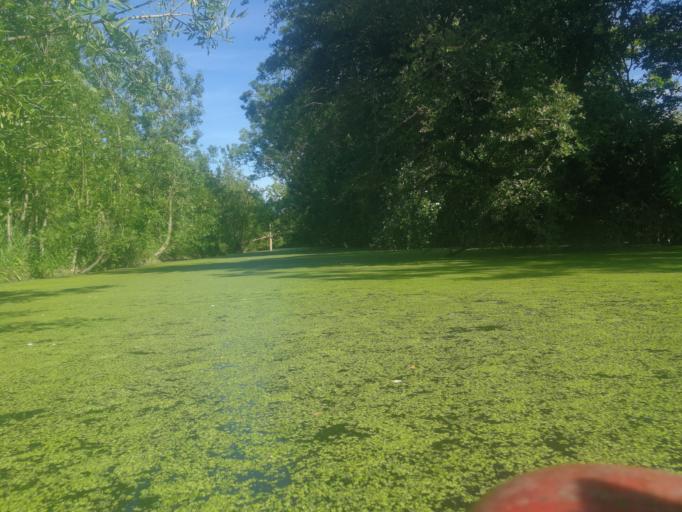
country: FR
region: Poitou-Charentes
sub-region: Departement de la Charente-Maritime
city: Marans
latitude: 46.3617
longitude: -0.9558
